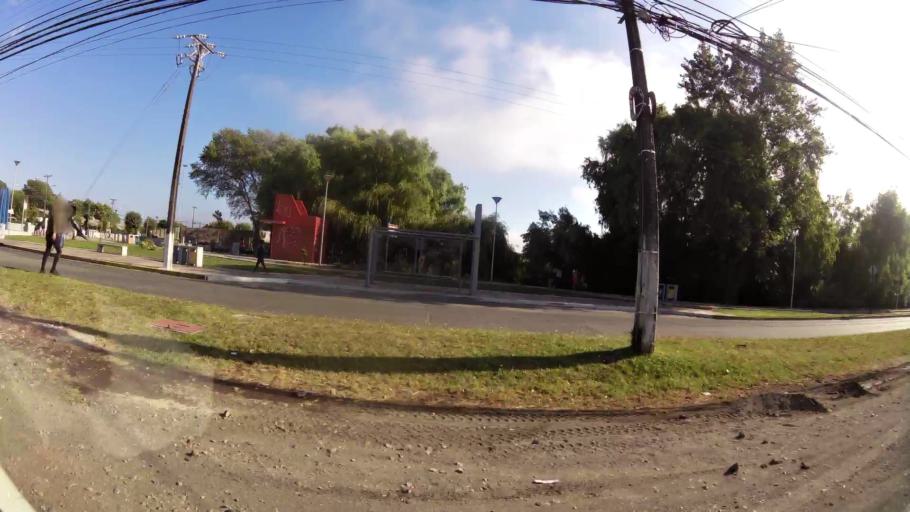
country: CL
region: Biobio
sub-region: Provincia de Concepcion
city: Concepcion
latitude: -36.8001
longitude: -73.0942
